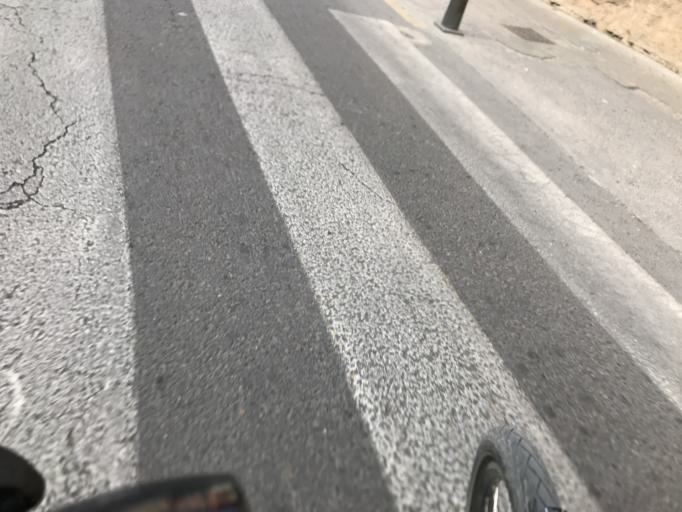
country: ES
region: Valencia
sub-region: Provincia de Valencia
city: Valencia
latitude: 39.4741
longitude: -0.3796
